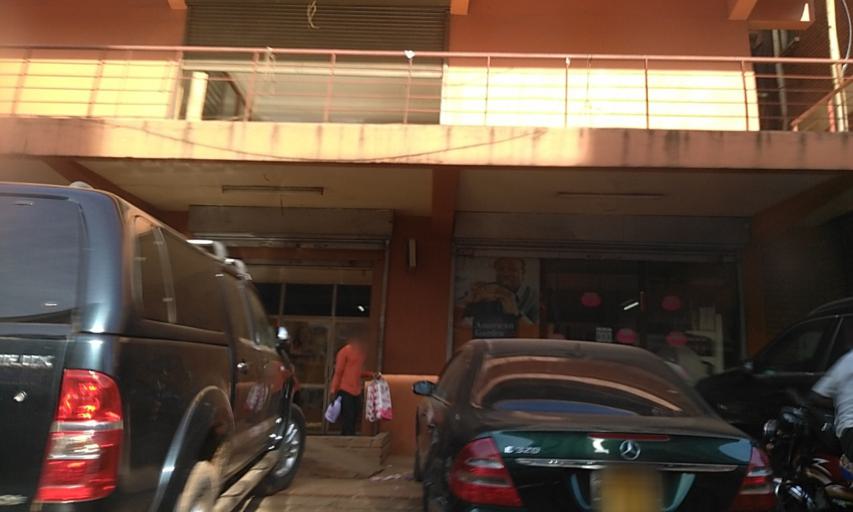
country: UG
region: Central Region
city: Kampala Central Division
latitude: 0.3151
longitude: 32.5717
